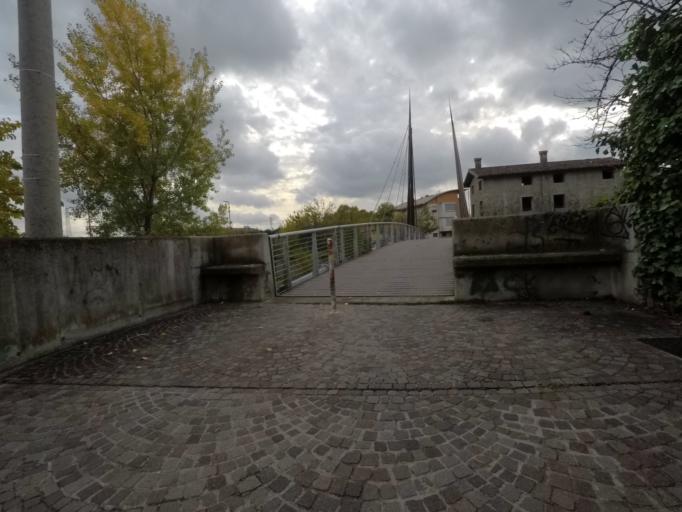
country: IT
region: Friuli Venezia Giulia
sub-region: Provincia di Udine
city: Colugna
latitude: 46.0821
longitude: 13.2051
